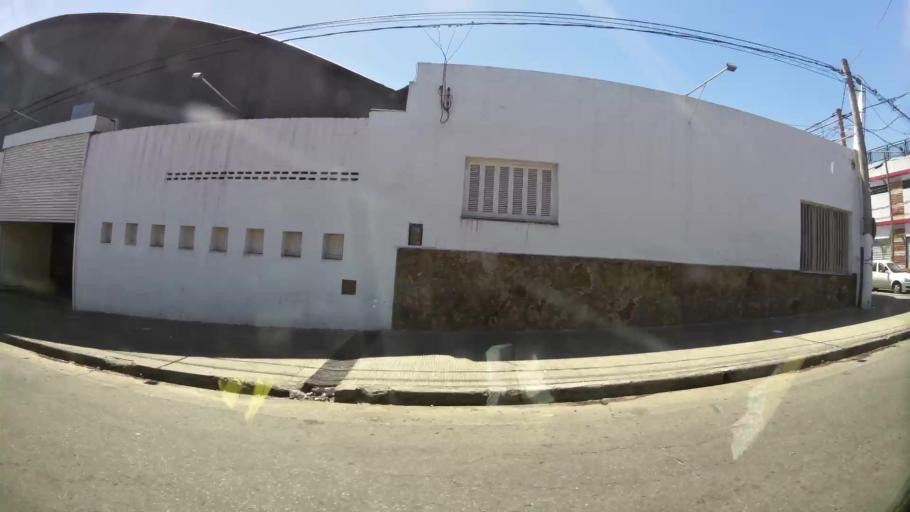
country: AR
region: Cordoba
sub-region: Departamento de Capital
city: Cordoba
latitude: -31.4273
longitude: -64.1510
